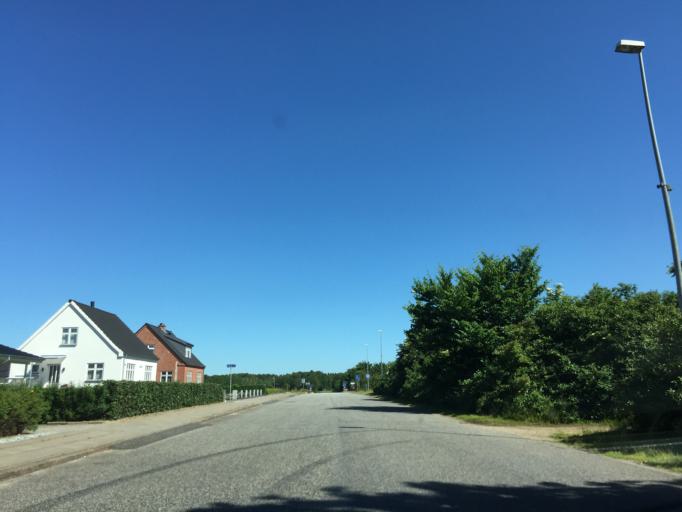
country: DK
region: Central Jutland
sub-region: Viborg Kommune
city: Bjerringbro
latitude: 56.3063
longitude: 9.5995
